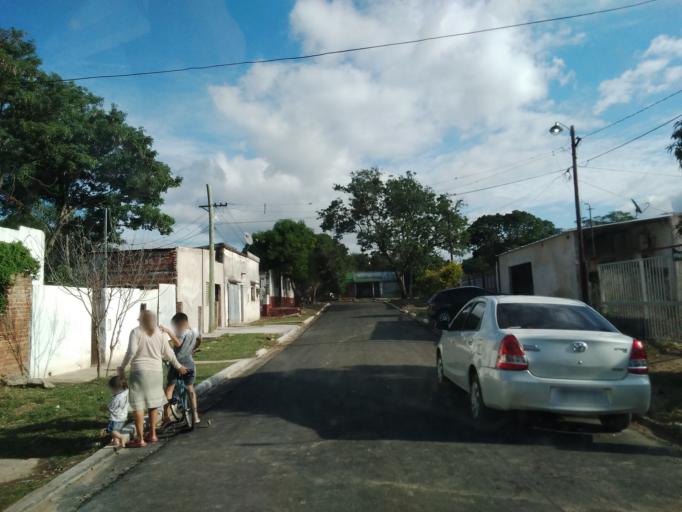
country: AR
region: Corrientes
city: Corrientes
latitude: -27.4623
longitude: -58.8144
